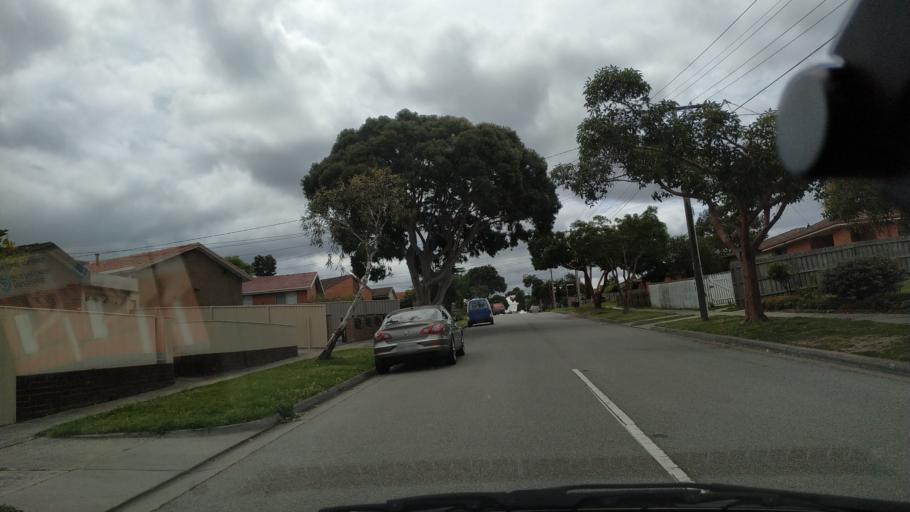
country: AU
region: Victoria
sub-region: Greater Dandenong
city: Noble Park North
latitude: -37.9576
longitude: 145.1967
